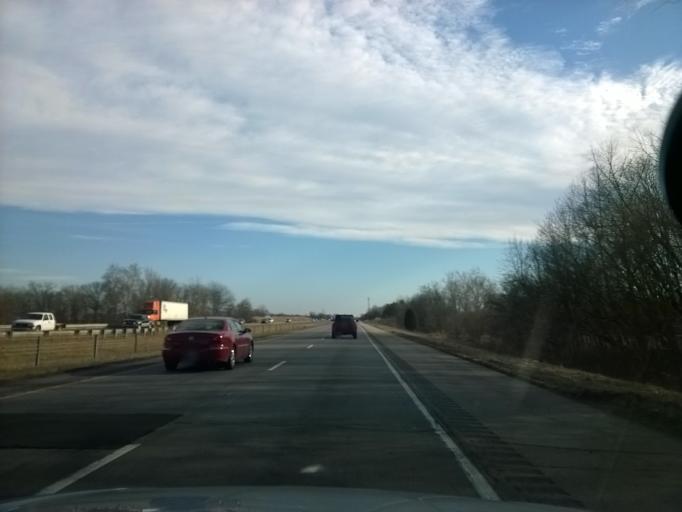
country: US
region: Indiana
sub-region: Johnson County
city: Edinburgh
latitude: 39.4344
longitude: -85.9806
